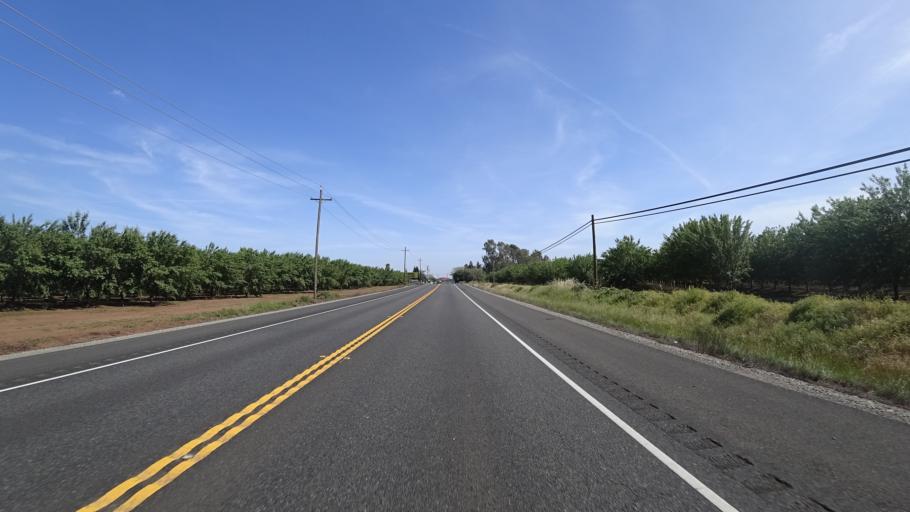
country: US
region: California
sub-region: Butte County
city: Chico
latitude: 39.8007
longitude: -121.9053
